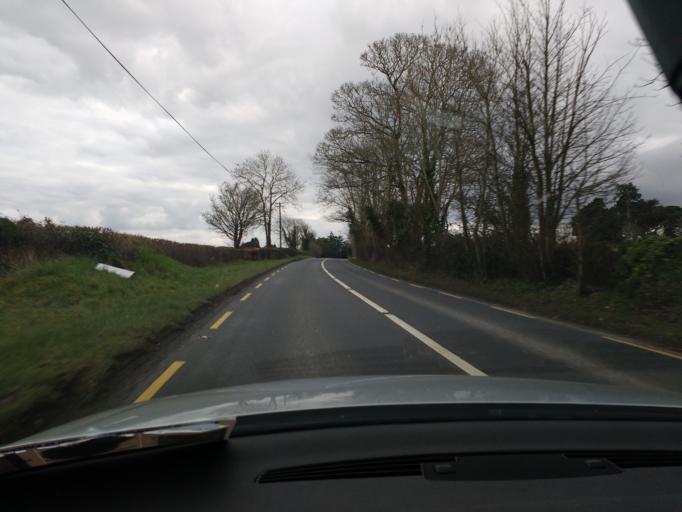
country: IE
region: Leinster
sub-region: Kilkenny
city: Kilkenny
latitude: 52.6846
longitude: -7.2749
